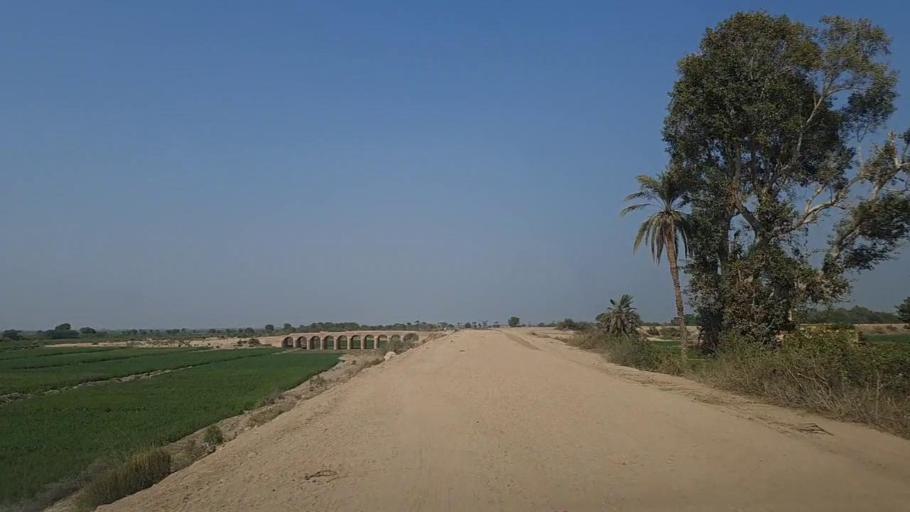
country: PK
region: Sindh
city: Naushahro Firoz
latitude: 26.8526
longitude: 67.9586
